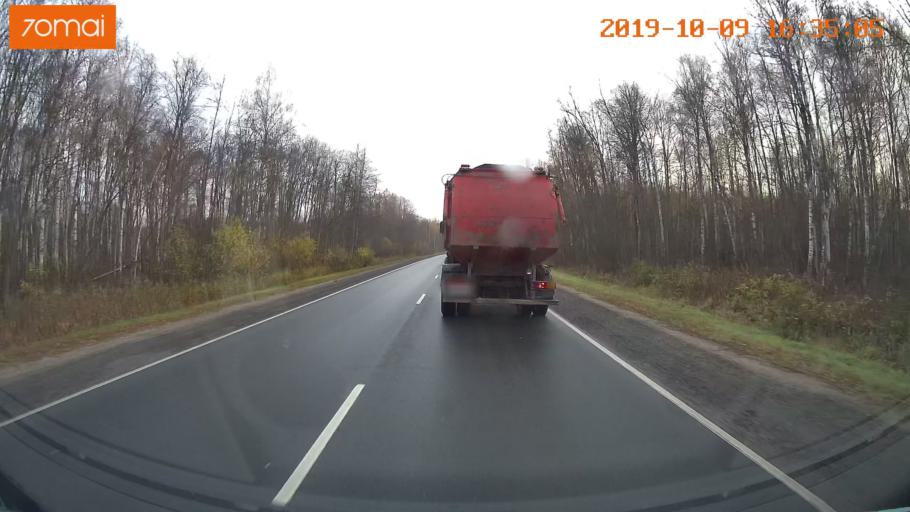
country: RU
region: Kostroma
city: Oktyabr'skiy
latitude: 57.5594
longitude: 40.9975
